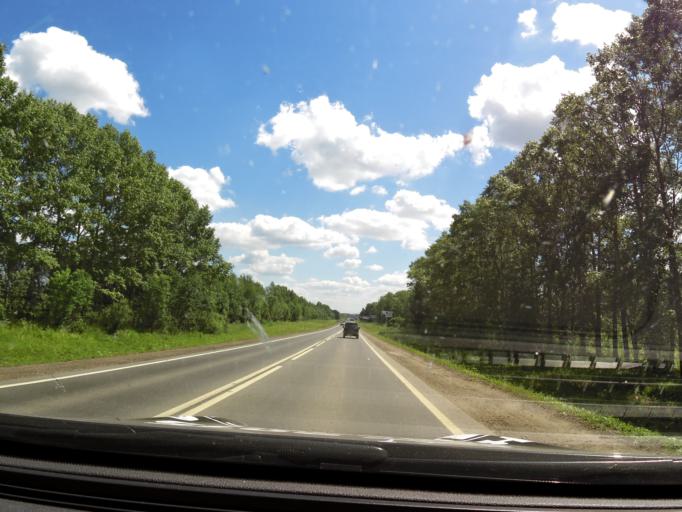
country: RU
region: Vologda
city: Molochnoye
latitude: 59.2579
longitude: 39.7539
